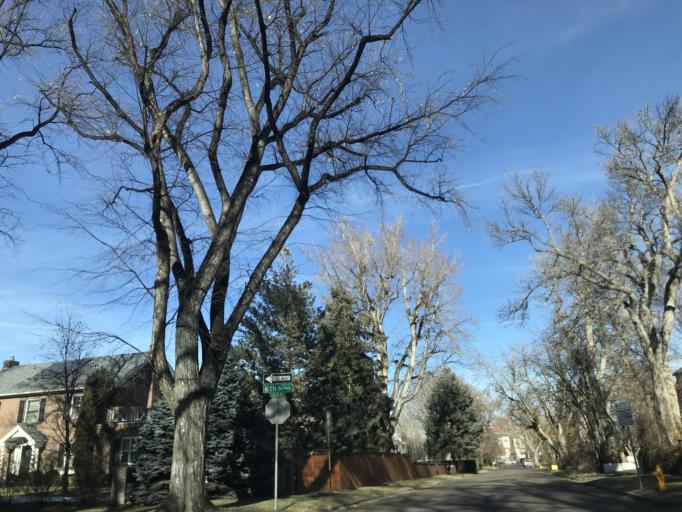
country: US
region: Colorado
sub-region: Arapahoe County
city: Glendale
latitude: 39.7256
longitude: -104.9360
